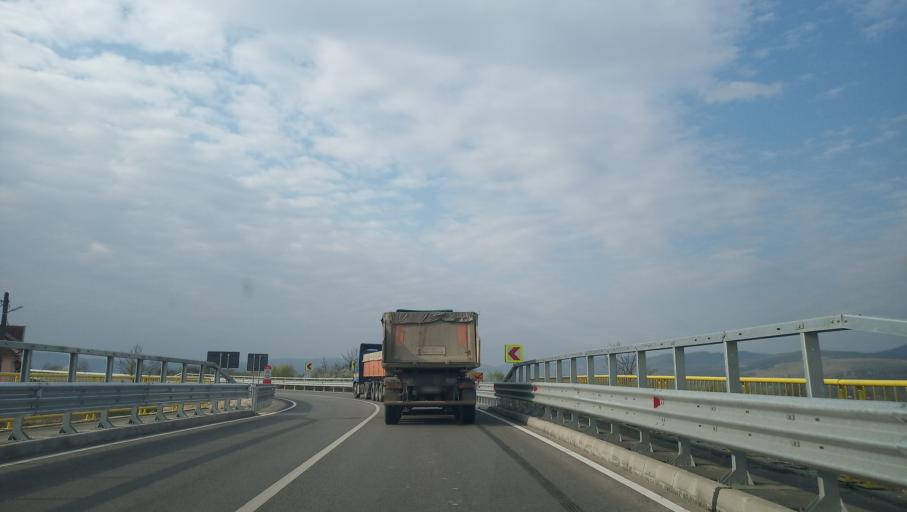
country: RO
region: Bihor
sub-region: Comuna Rieni
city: Rieni
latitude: 46.5724
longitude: 22.4405
